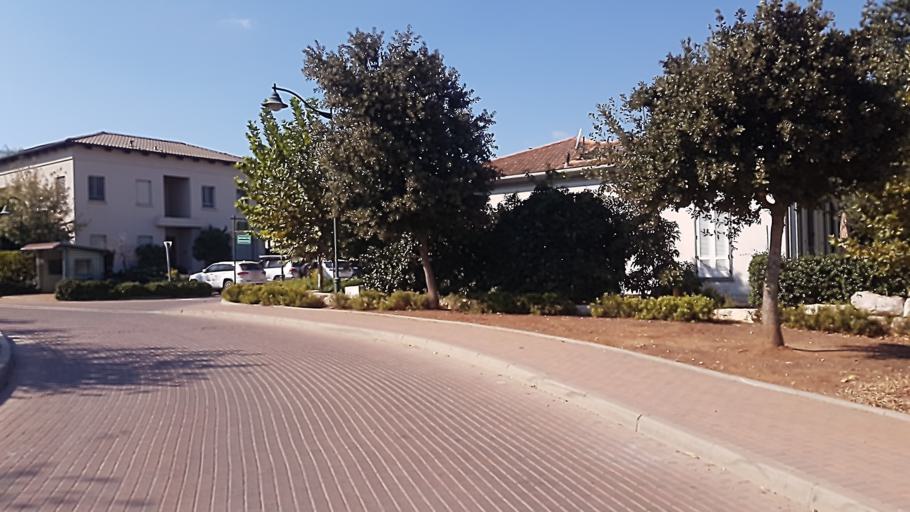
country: IL
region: Central District
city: Ra'anana
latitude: 32.2127
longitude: 34.8965
